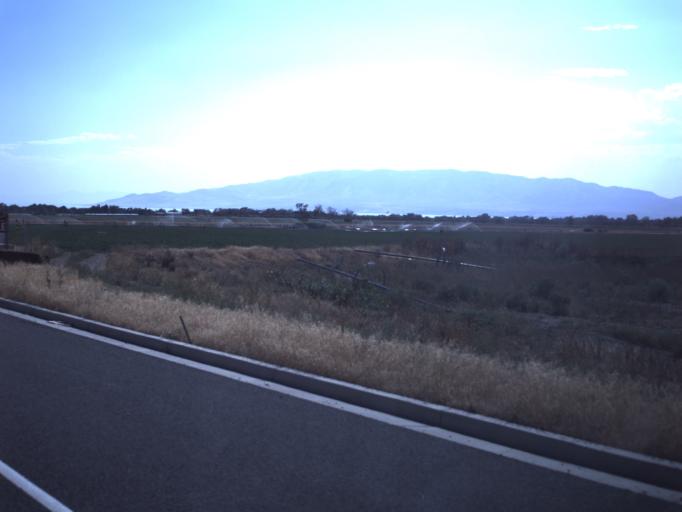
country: US
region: Utah
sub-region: Utah County
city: Cedar Hills
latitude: 40.4106
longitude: -111.7735
